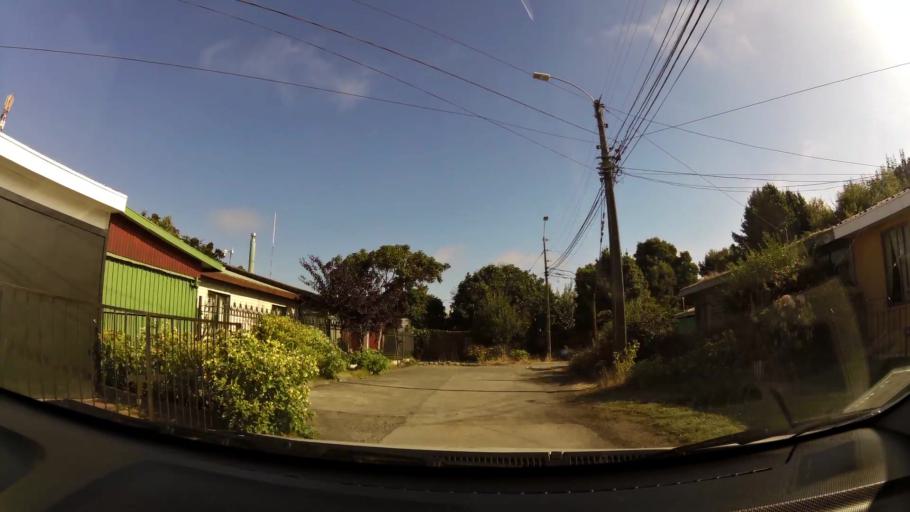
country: CL
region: Biobio
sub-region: Provincia de Concepcion
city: Concepcion
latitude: -36.7984
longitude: -73.0908
